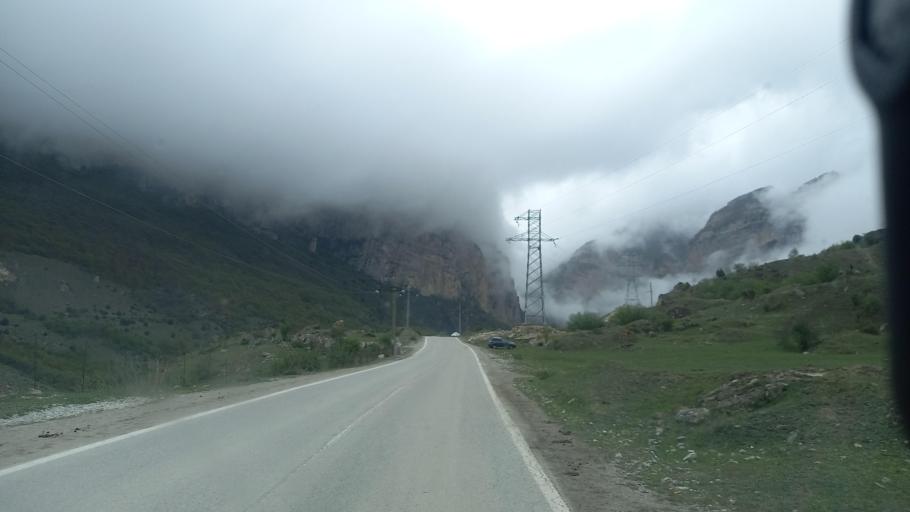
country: RU
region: Kabardino-Balkariya
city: Verkhnyaya Balkariya
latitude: 43.1694
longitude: 43.4993
